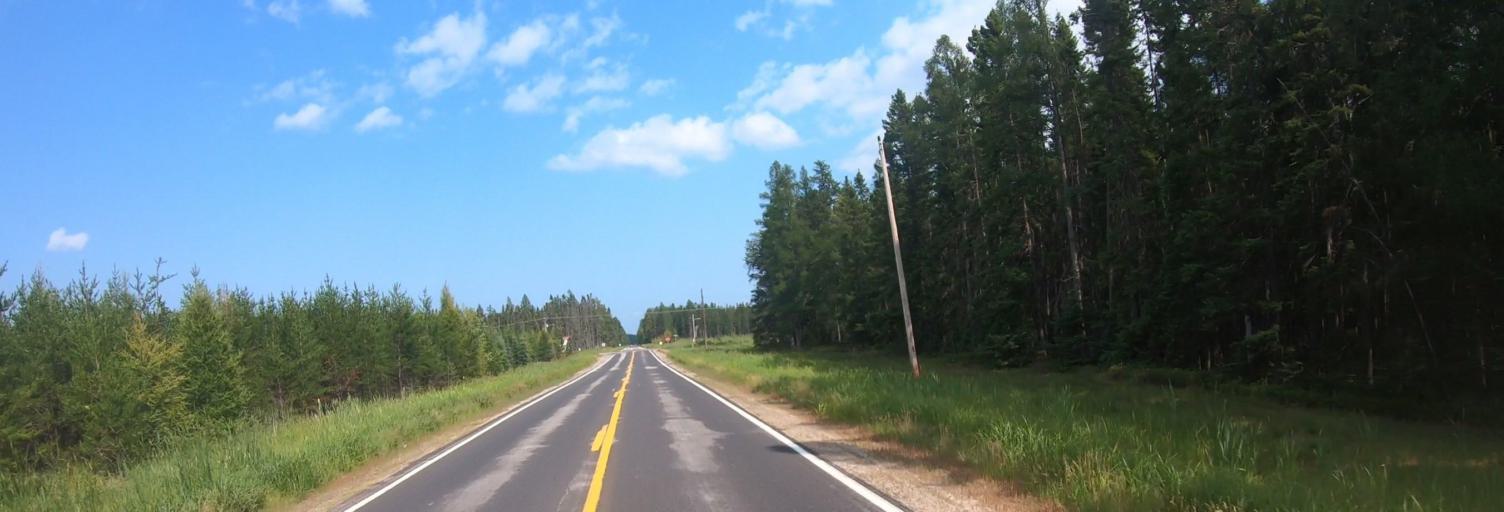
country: US
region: Minnesota
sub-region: Saint Louis County
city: Mountain Iron
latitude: 47.8911
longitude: -92.6622
